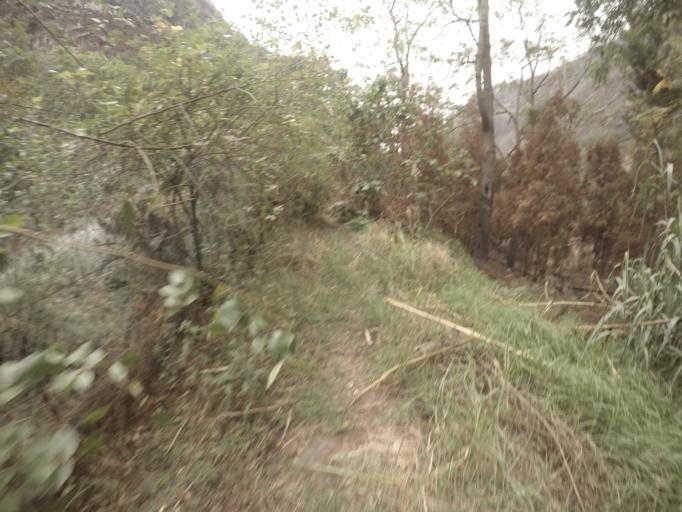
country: PT
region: Madeira
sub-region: Funchal
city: Nossa Senhora do Monte
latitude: 32.6933
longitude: -16.9161
